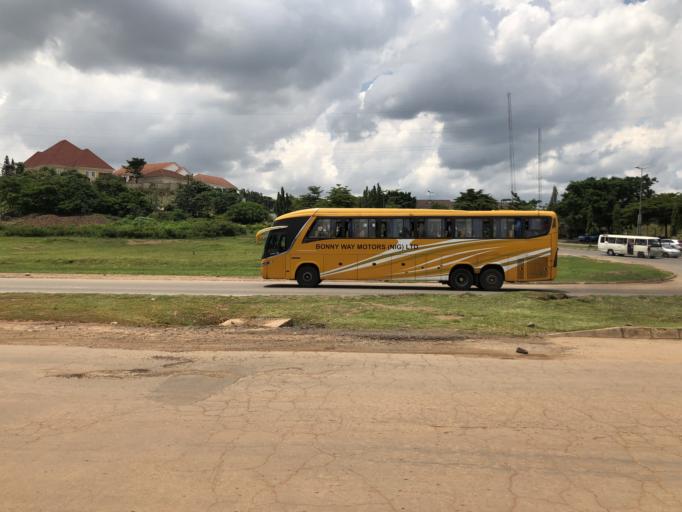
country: NG
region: Abuja Federal Capital Territory
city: Abuja
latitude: 9.0484
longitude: 7.5158
